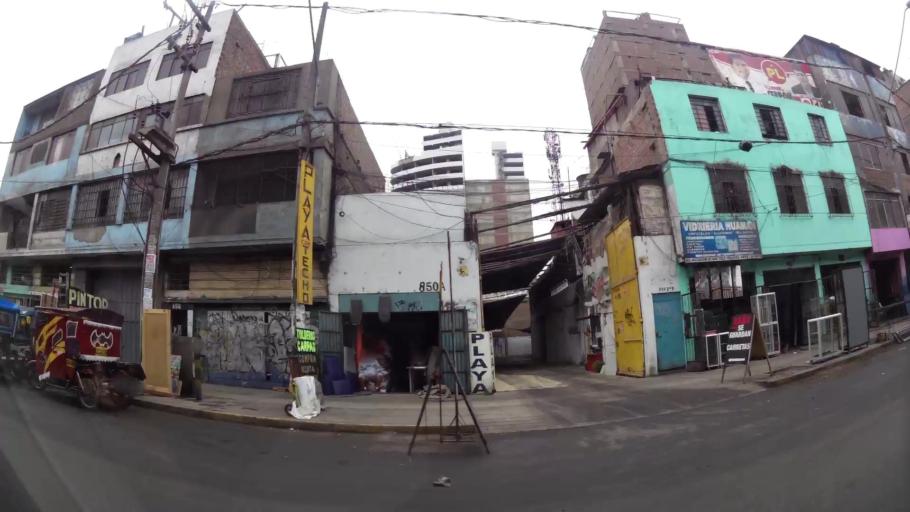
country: PE
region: Lima
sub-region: Lima
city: San Luis
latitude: -12.0697
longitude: -77.0120
